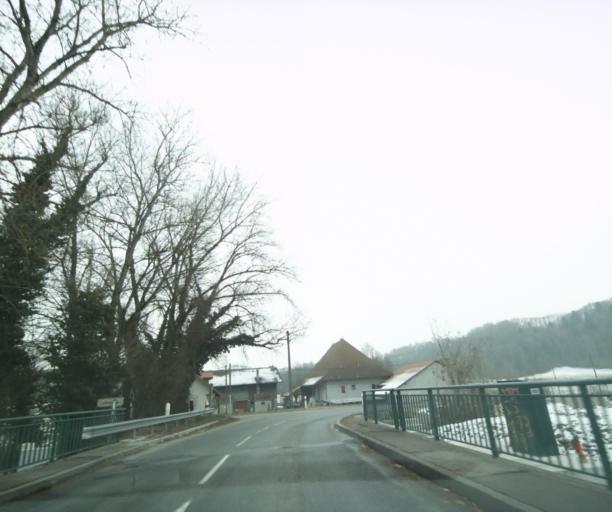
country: FR
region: Rhone-Alpes
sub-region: Departement de la Haute-Savoie
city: Arthaz-Pont-Notre-Dame
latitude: 46.1502
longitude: 6.2711
